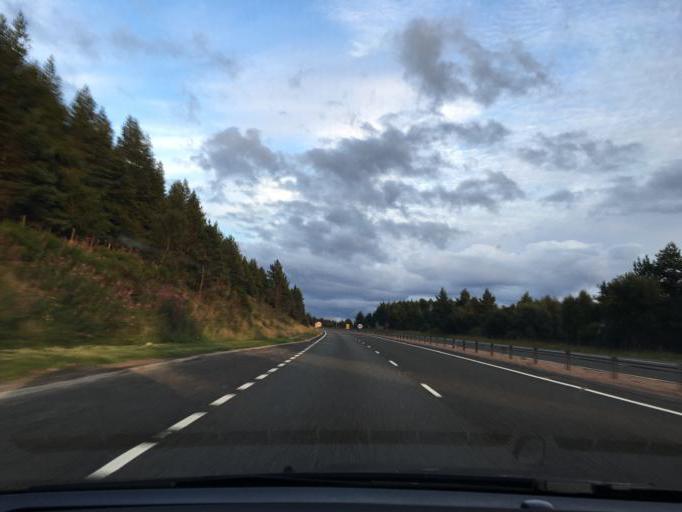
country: GB
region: Scotland
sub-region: Highland
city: Aviemore
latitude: 57.3168
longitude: -3.9656
